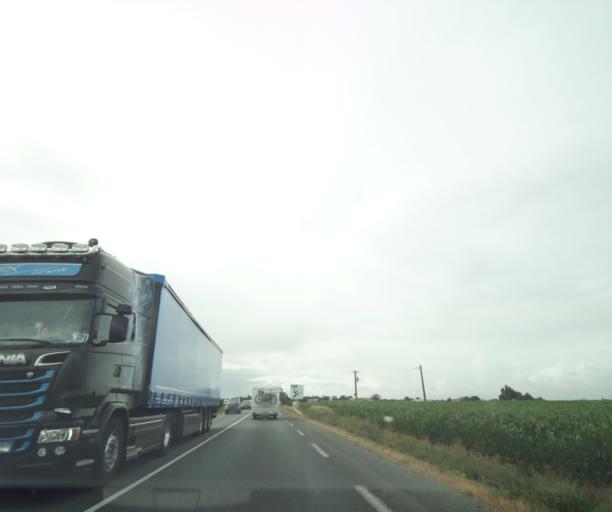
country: FR
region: Pays de la Loire
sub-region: Departement de la Vendee
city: Champagne-les-Marais
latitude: 46.4289
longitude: -1.0937
